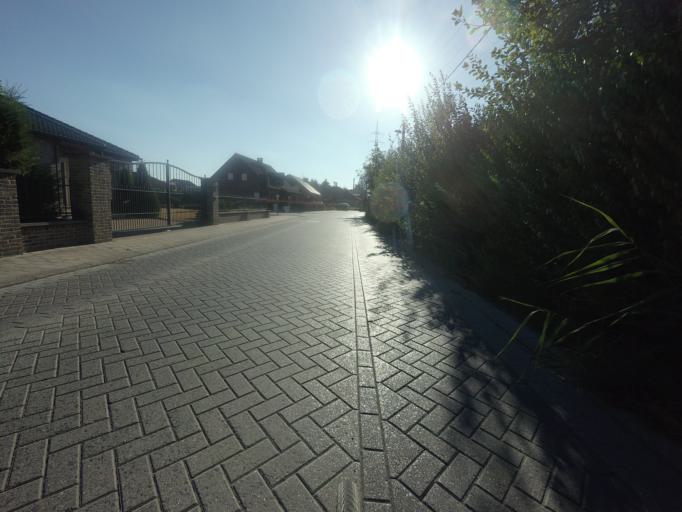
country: BE
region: Flanders
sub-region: Provincie Antwerpen
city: Beerse
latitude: 51.3240
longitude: 4.8308
